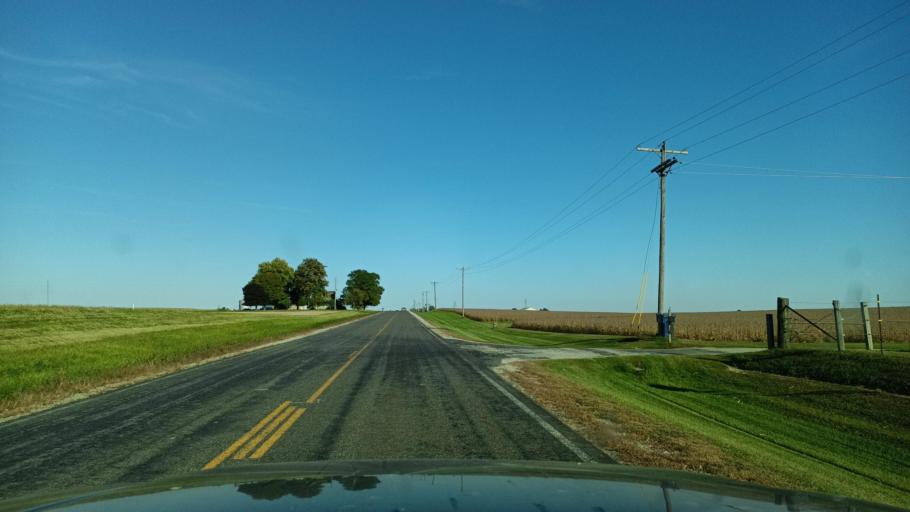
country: US
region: Illinois
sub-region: De Witt County
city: Farmer City
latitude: 40.2240
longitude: -88.7396
